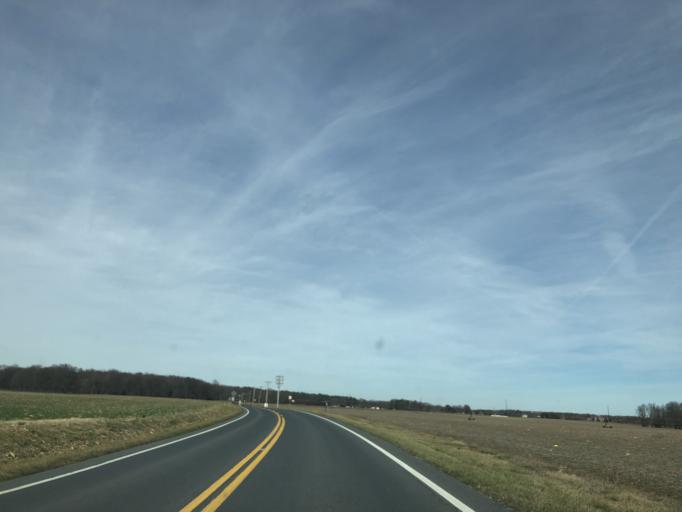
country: US
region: Delaware
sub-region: Kent County
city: Dover Base Housing
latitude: 39.1190
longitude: -75.4441
